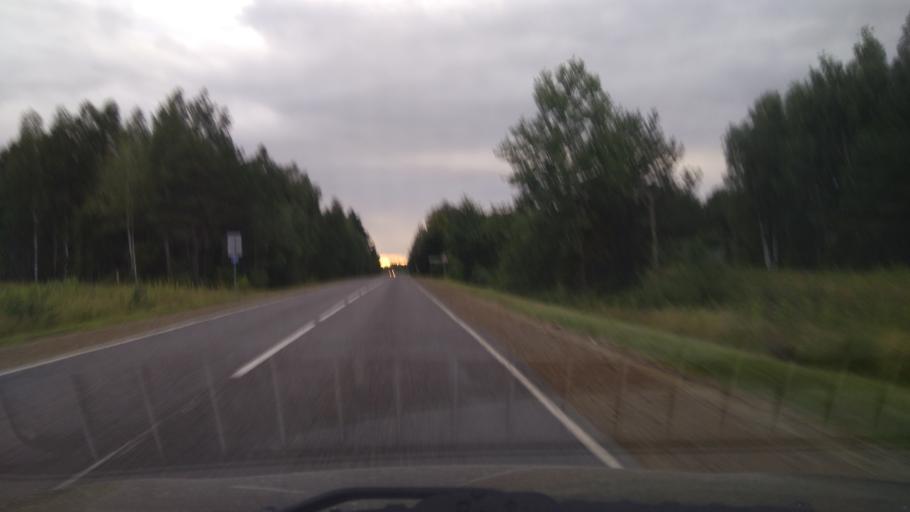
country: BY
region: Brest
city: Byaroza
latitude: 52.4144
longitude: 24.9870
